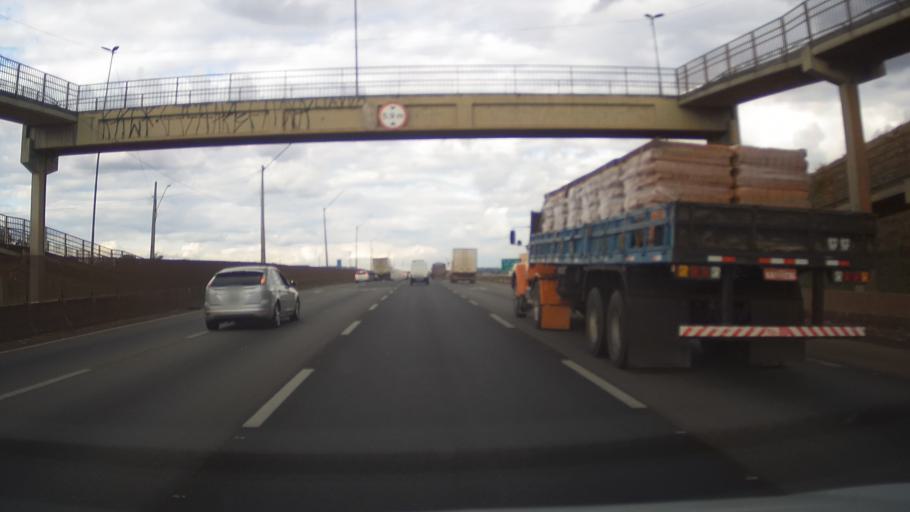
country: BR
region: Minas Gerais
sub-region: Betim
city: Betim
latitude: -19.9589
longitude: -44.1516
